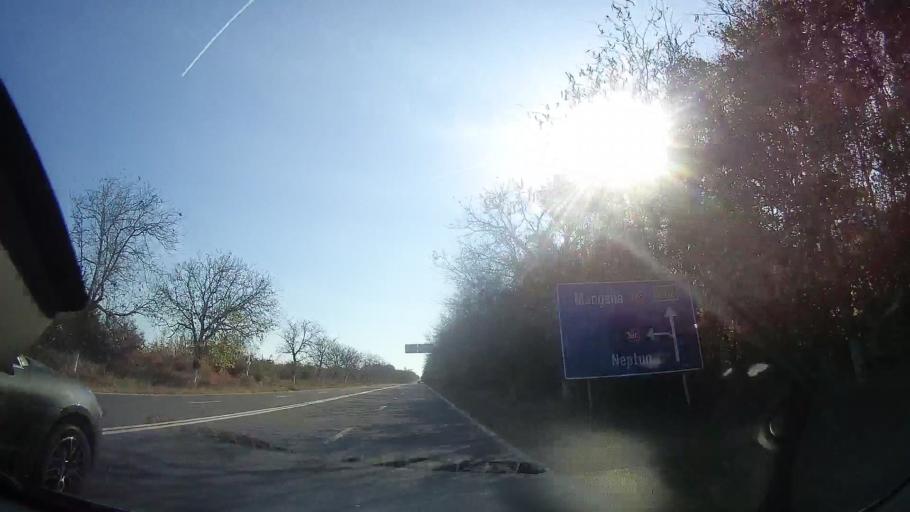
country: RO
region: Constanta
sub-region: Comuna Douazeci si Trei August
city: Dulcesti
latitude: 43.8819
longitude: 28.5733
